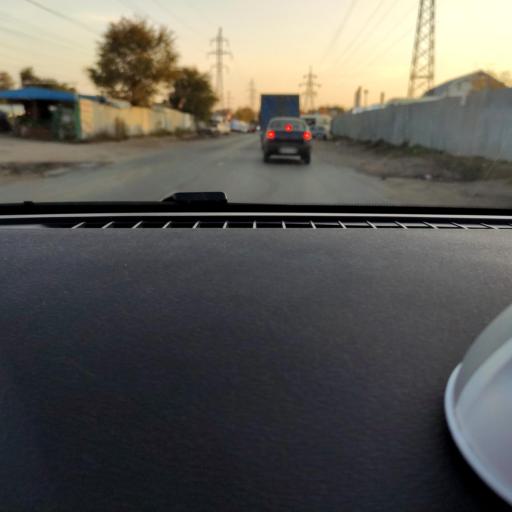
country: RU
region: Samara
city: Petra-Dubrava
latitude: 53.2567
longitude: 50.2953
